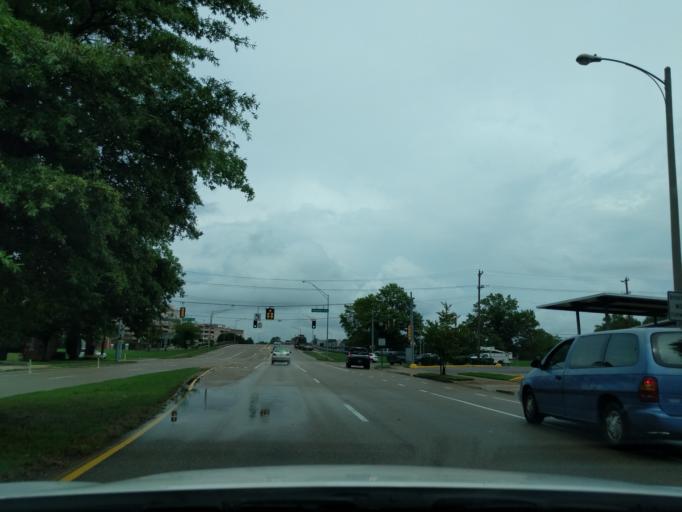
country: US
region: Tennessee
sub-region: Shelby County
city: Memphis
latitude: 35.1500
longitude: -90.0421
